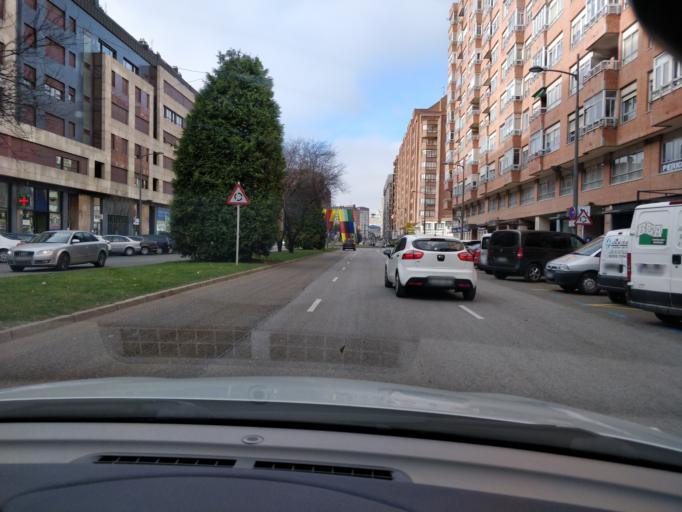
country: ES
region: Castille and Leon
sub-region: Provincia de Burgos
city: Burgos
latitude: 42.3455
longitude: -3.6909
